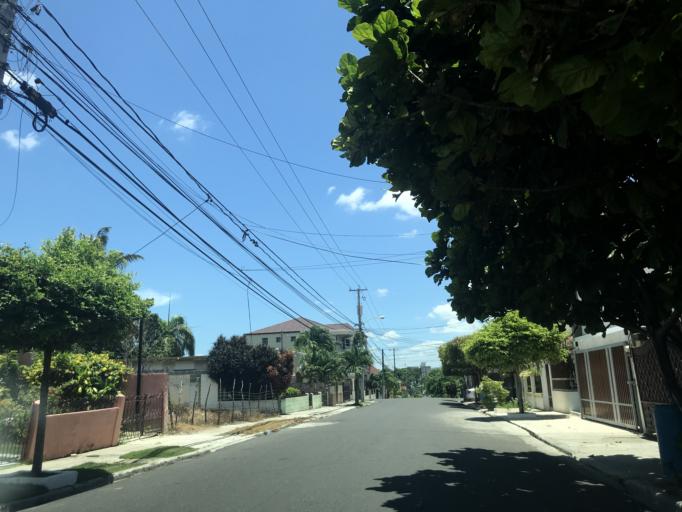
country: DO
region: Santiago
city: Santiago de los Caballeros
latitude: 19.4403
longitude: -70.6961
